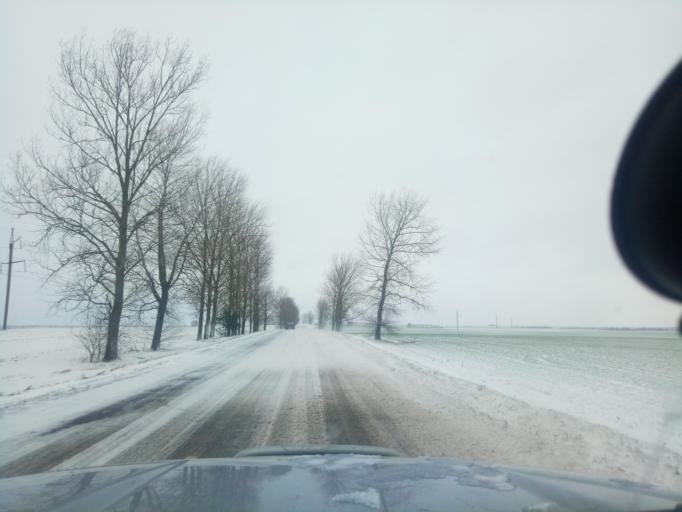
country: BY
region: Minsk
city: Tsimkavichy
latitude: 53.0542
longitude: 26.9371
